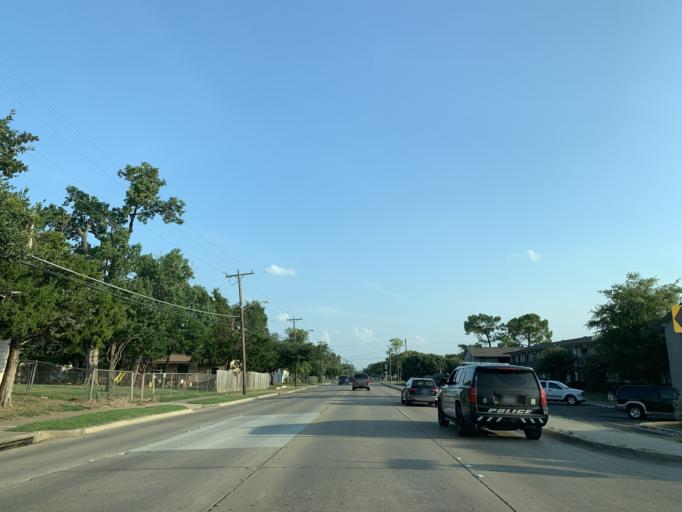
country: US
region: Texas
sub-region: Tarrant County
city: Hurst
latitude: 32.8203
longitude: -97.1865
